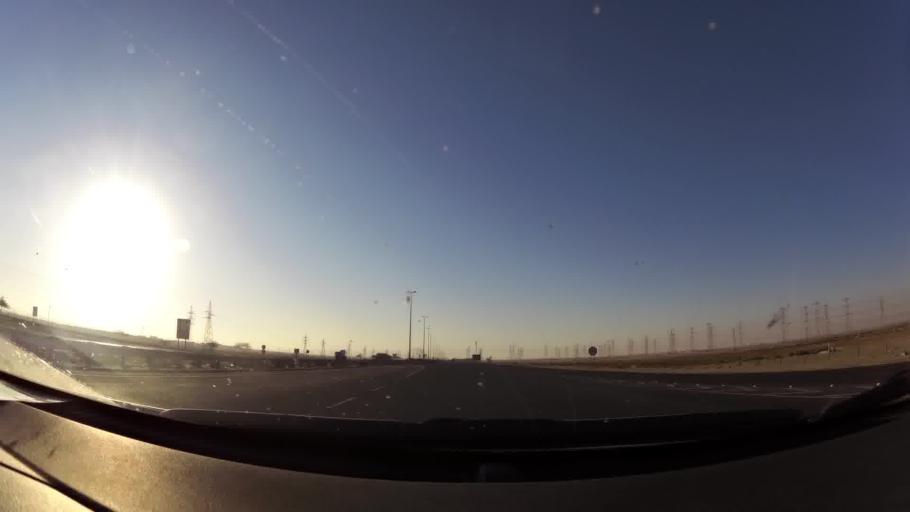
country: KW
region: Al Ahmadi
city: Al Fahahil
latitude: 28.7755
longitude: 48.2763
